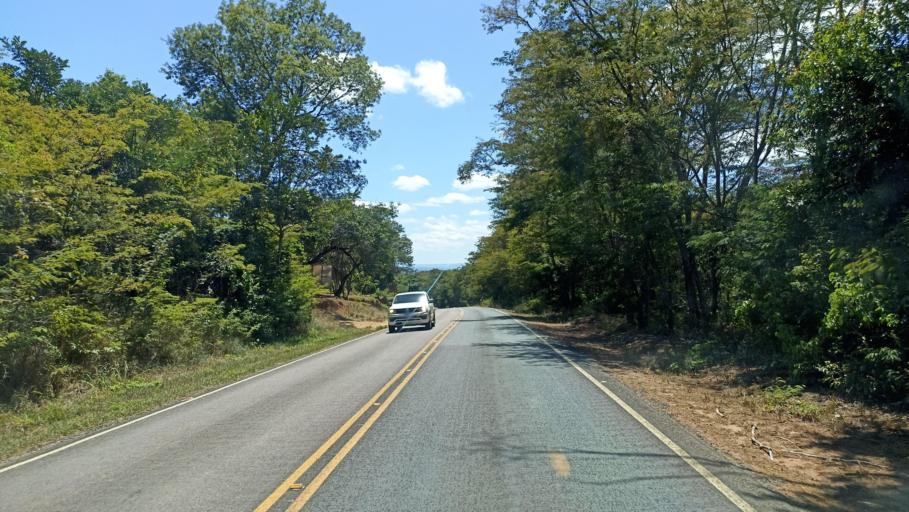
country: BR
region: Bahia
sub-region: Andarai
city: Vera Cruz
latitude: -12.7860
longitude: -41.3286
